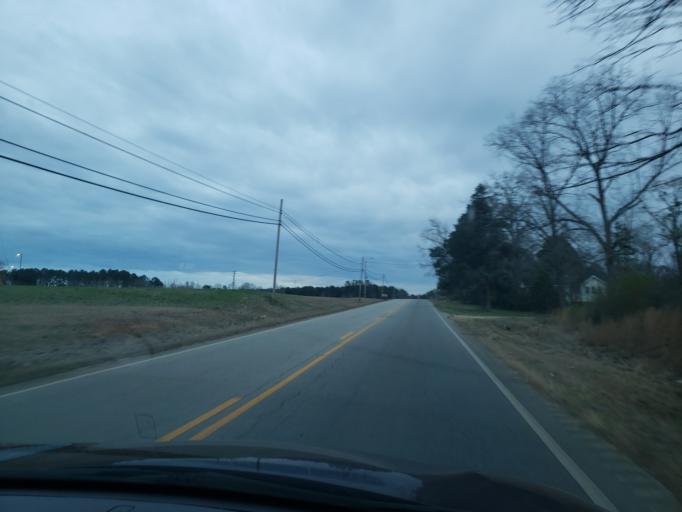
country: US
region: Alabama
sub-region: Chambers County
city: Lafayette
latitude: 32.9159
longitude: -85.3993
